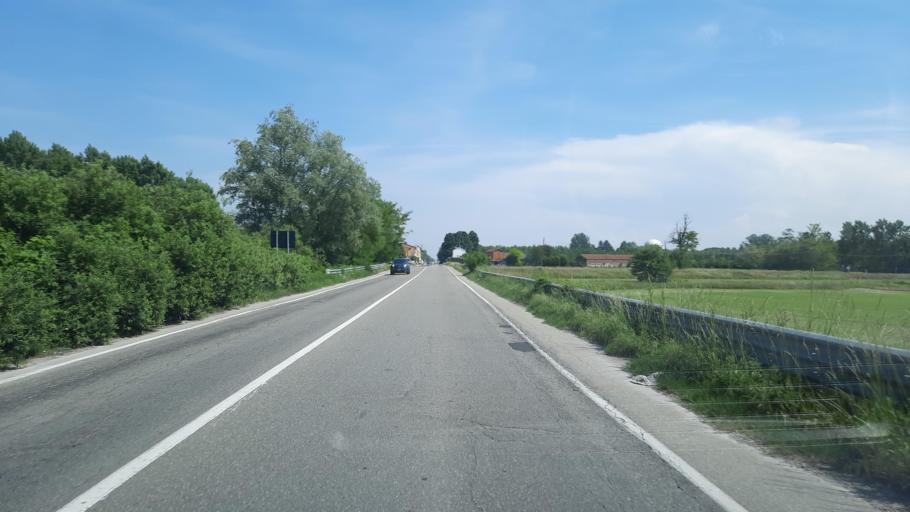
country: IT
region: Lombardy
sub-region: Provincia di Pavia
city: Cergnago
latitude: 45.2359
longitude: 8.7967
